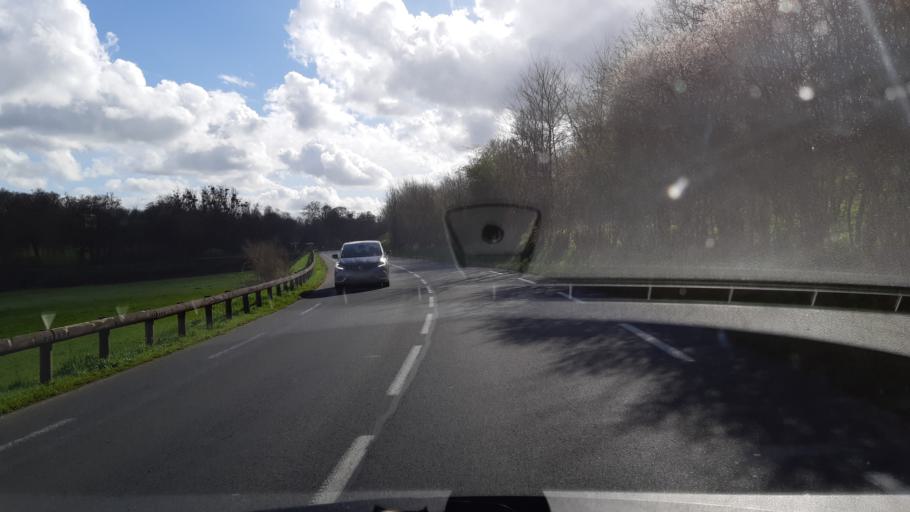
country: FR
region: Lower Normandy
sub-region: Departement de la Manche
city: Agneaux
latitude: 49.0834
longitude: -1.1167
